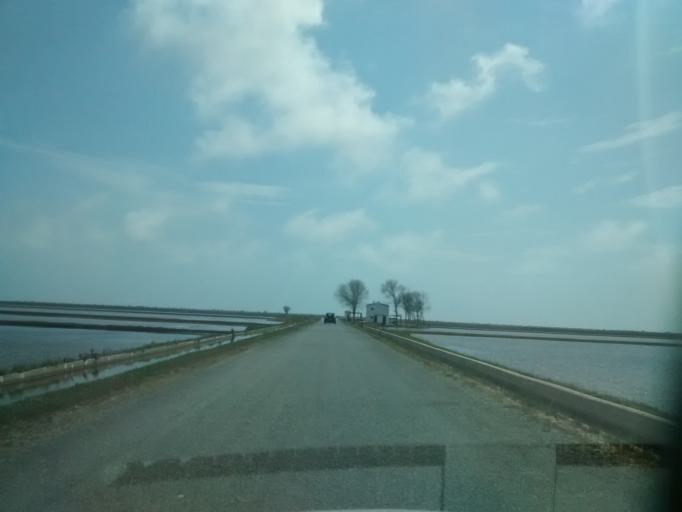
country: ES
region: Catalonia
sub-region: Provincia de Tarragona
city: Deltebre
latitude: 40.6795
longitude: 0.7976
